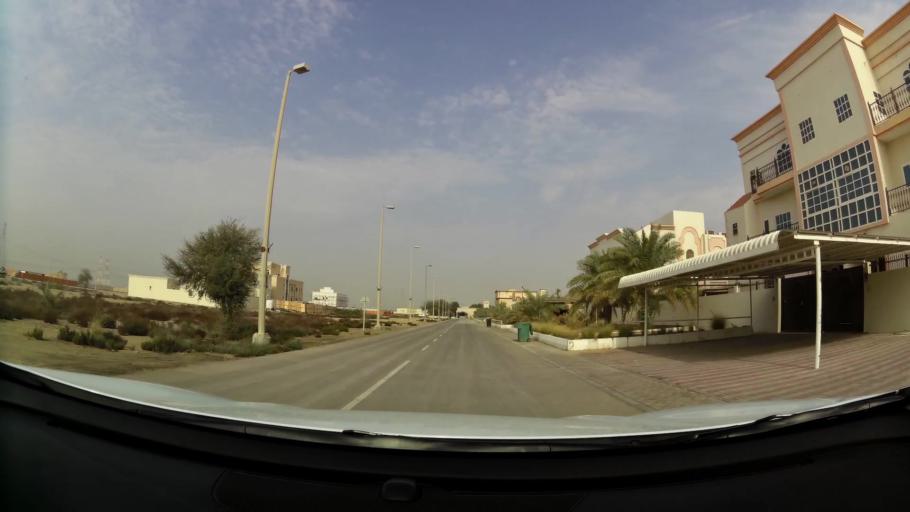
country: AE
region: Abu Dhabi
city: Abu Dhabi
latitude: 24.6665
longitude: 54.7534
